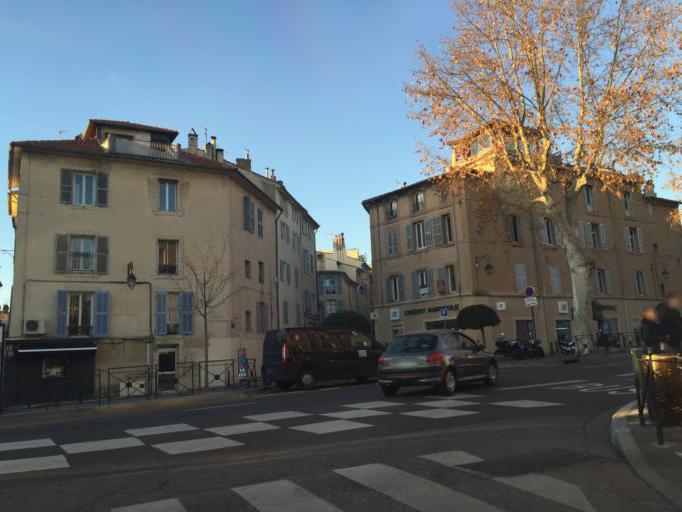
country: FR
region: Provence-Alpes-Cote d'Azur
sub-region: Departement des Bouches-du-Rhone
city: Aix-en-Provence
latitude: 43.5247
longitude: 5.4544
